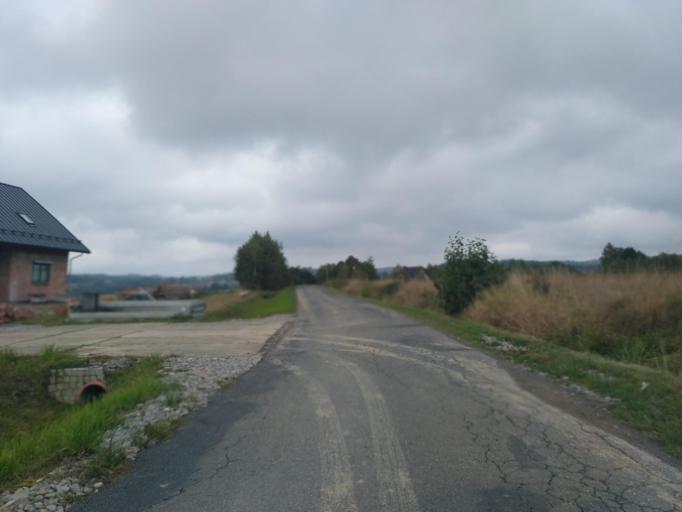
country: PL
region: Subcarpathian Voivodeship
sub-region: Powiat debicki
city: Brzostek
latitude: 49.9322
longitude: 21.4478
